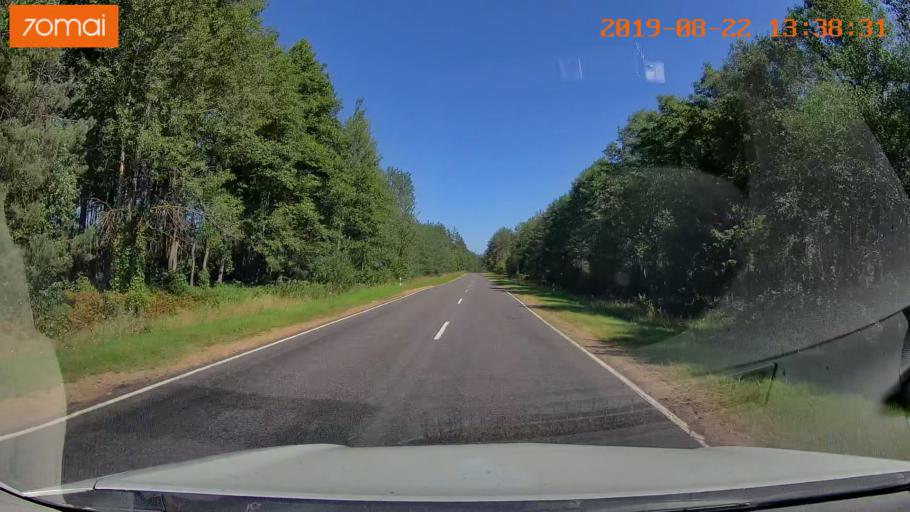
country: BY
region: Minsk
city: Staryya Darohi
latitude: 53.2243
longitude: 28.3254
